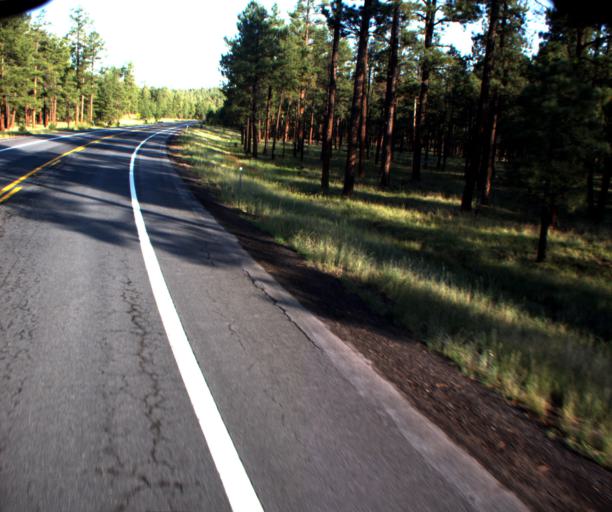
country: US
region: New Mexico
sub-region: Catron County
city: Reserve
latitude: 33.8119
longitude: -109.0681
